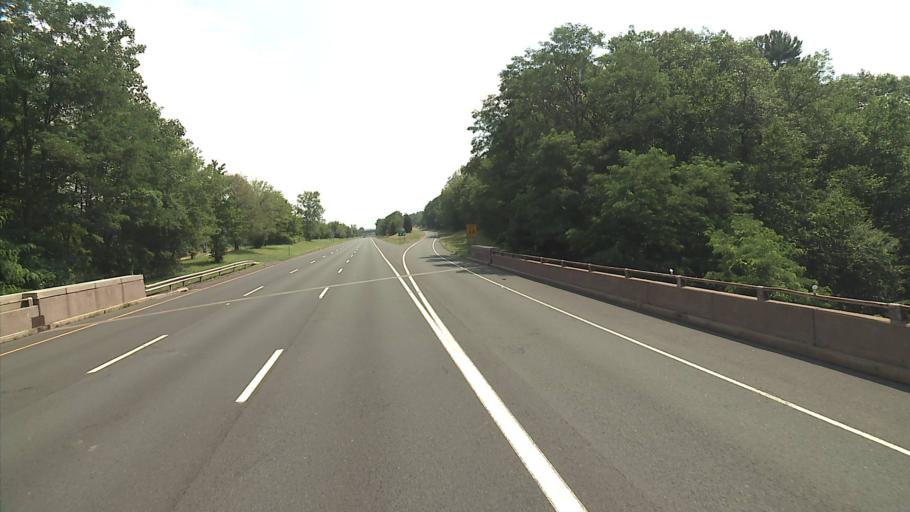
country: US
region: Connecticut
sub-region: Hartford County
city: Manchester
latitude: 41.7626
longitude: -72.4973
